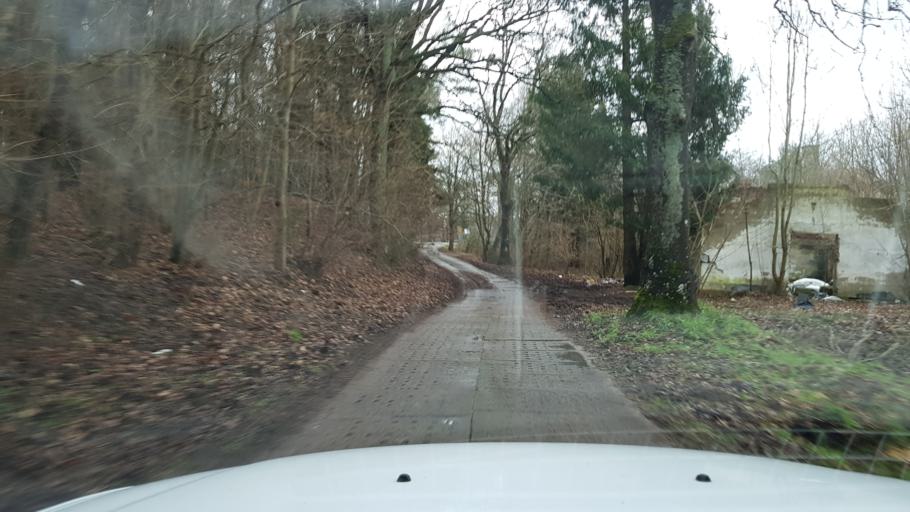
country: PL
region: West Pomeranian Voivodeship
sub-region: Powiat kolobrzeski
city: Grzybowo
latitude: 54.0761
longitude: 15.4339
